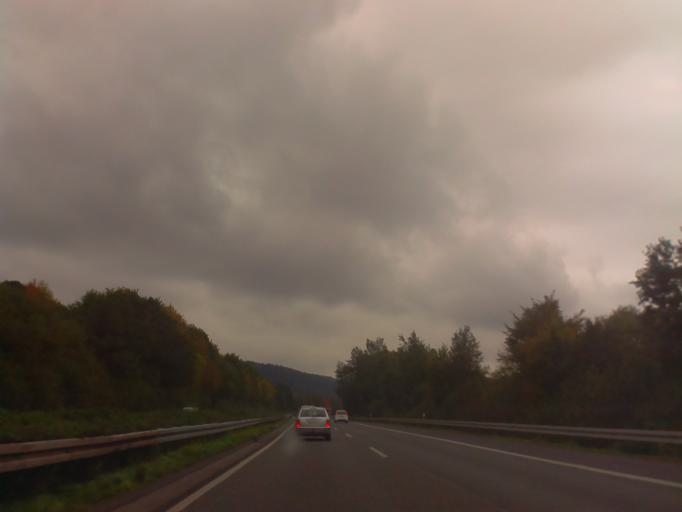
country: DE
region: Hesse
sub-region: Regierungsbezirk Darmstadt
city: Gelnhausen
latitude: 50.2184
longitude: 9.2405
